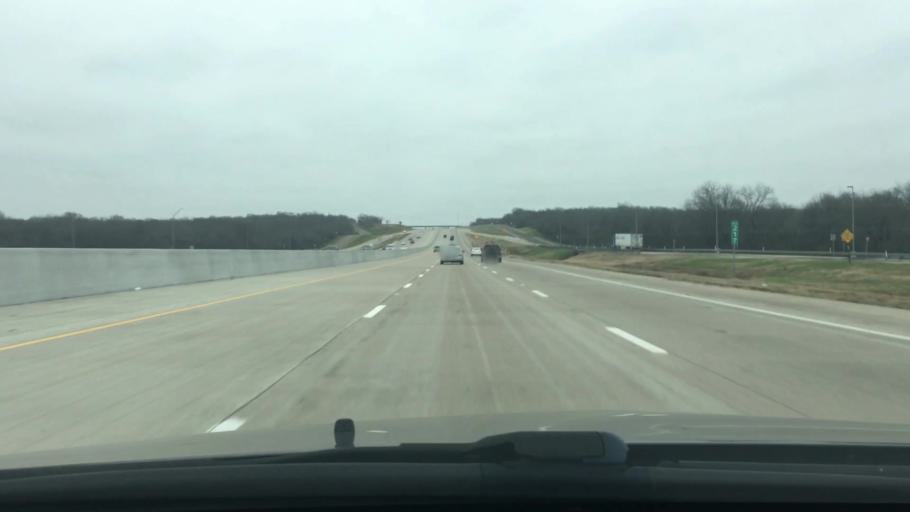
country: US
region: Texas
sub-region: Freestone County
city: Wortham
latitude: 31.9105
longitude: -96.3934
